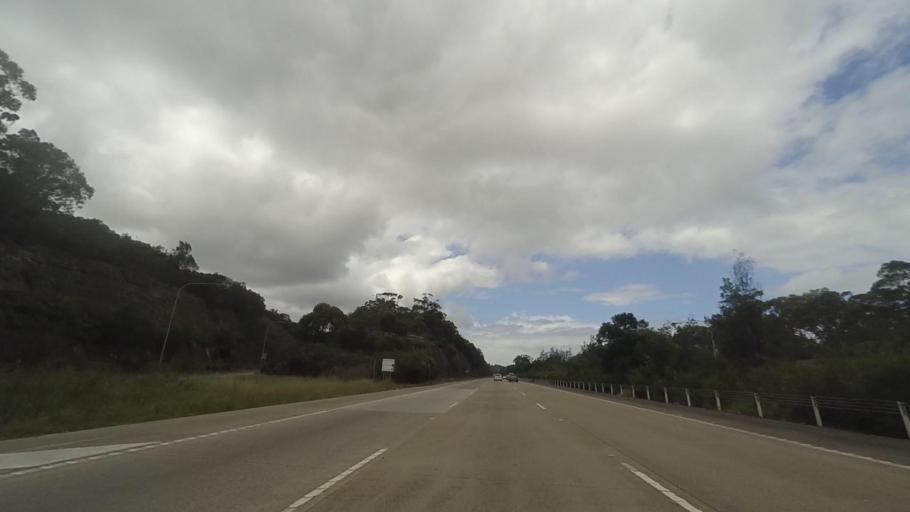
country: AU
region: New South Wales
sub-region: Gosford Shire
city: Point Clare
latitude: -33.4260
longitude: 151.2798
